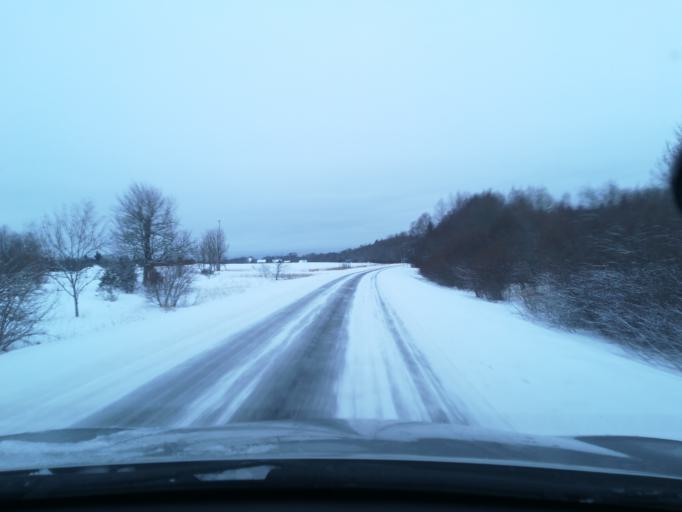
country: EE
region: Harju
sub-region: Keila linn
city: Keila
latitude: 59.3687
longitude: 24.3209
